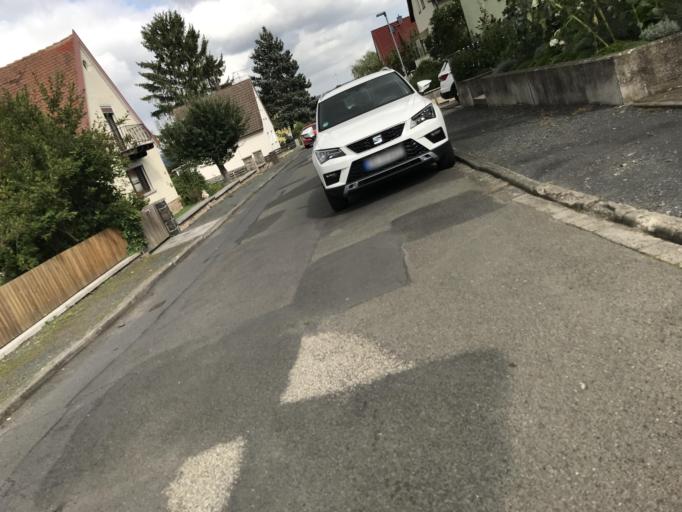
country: DE
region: Hesse
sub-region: Regierungsbezirk Giessen
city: Lauterbach
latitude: 50.6331
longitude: 9.3888
